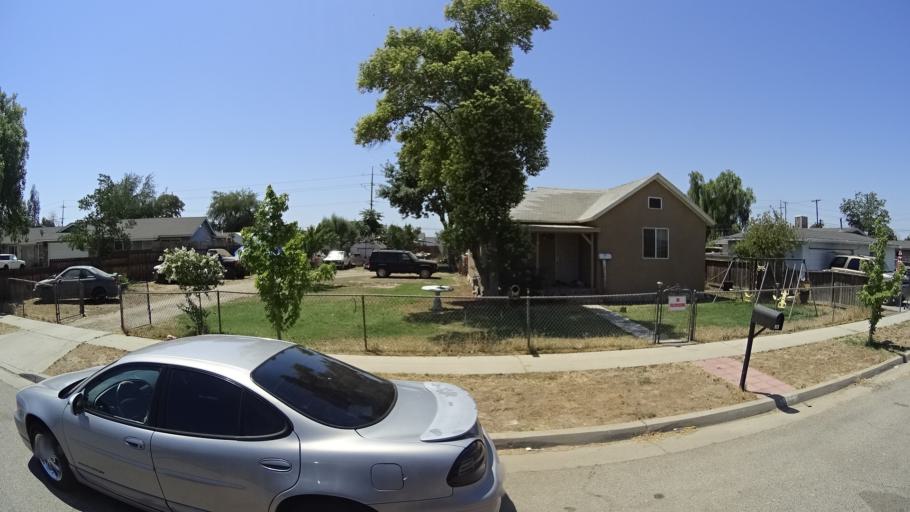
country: US
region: California
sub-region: Fresno County
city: West Park
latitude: 36.7077
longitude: -119.8125
